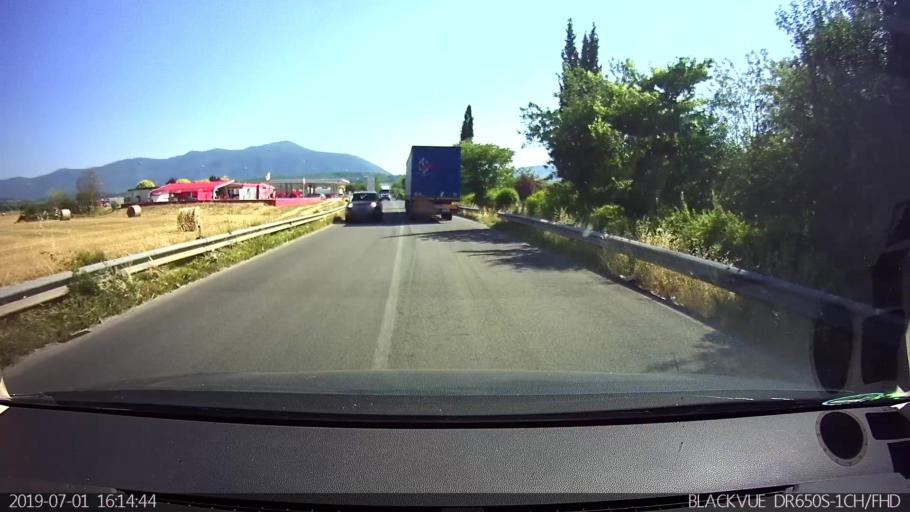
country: IT
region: Latium
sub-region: Provincia di Frosinone
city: Ceccano
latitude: 41.5995
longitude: 13.2933
